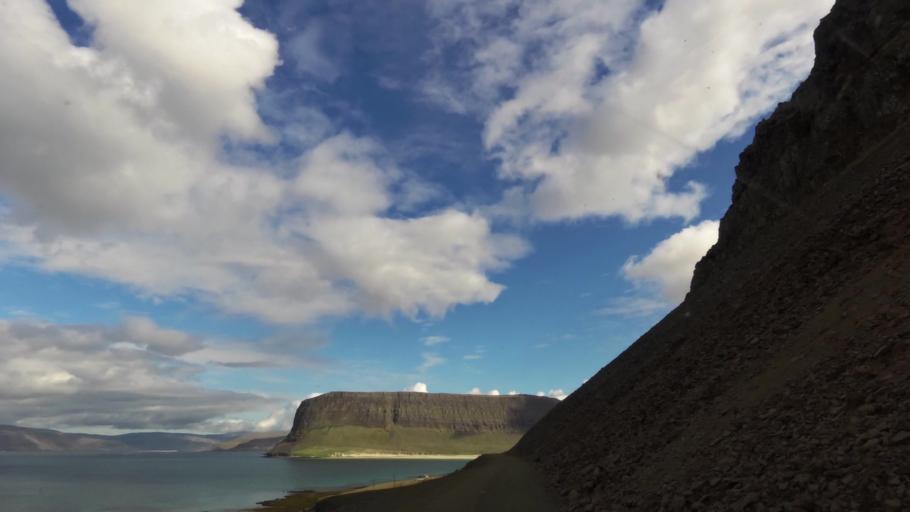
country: IS
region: West
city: Olafsvik
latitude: 65.5969
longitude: -24.1322
